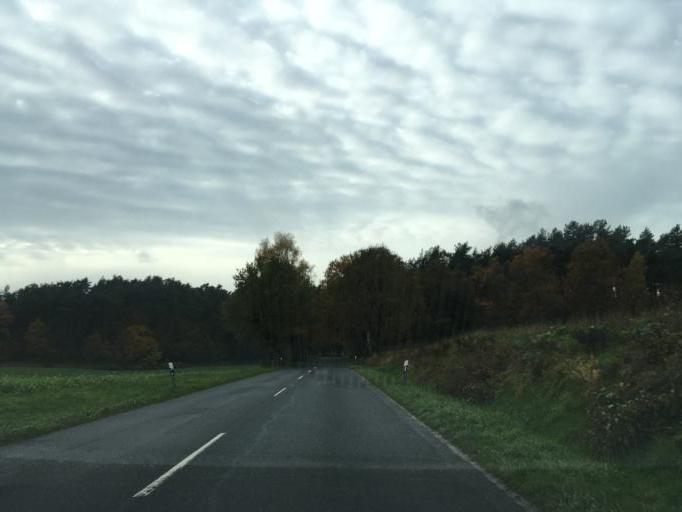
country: DE
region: Lower Saxony
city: Eyendorf
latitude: 53.1755
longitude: 10.1719
